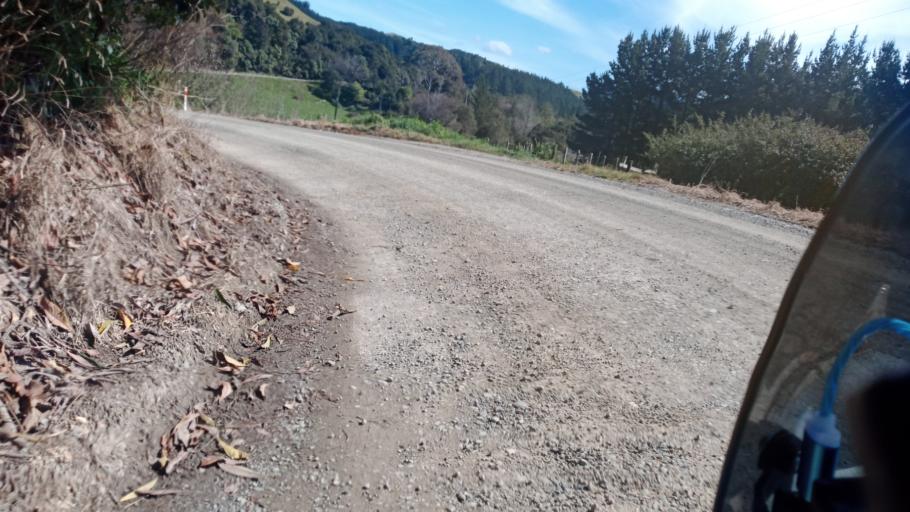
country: NZ
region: Gisborne
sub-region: Gisborne District
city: Gisborne
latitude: -37.9893
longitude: 178.2883
